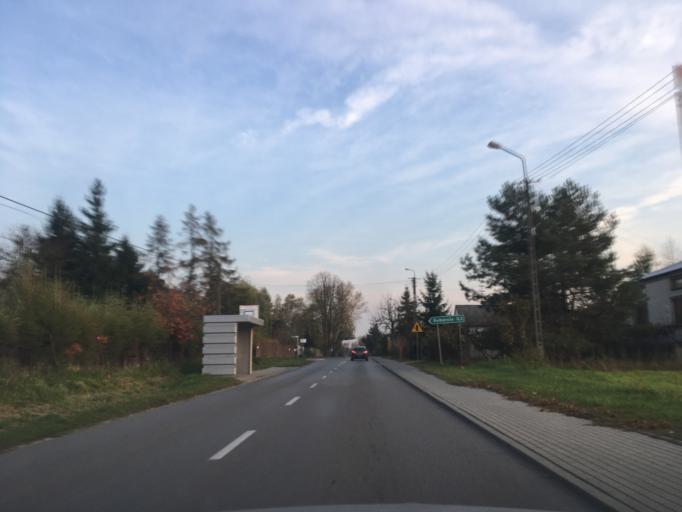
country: PL
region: Masovian Voivodeship
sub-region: Powiat piaseczynski
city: Lesznowola
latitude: 52.0550
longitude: 20.9244
